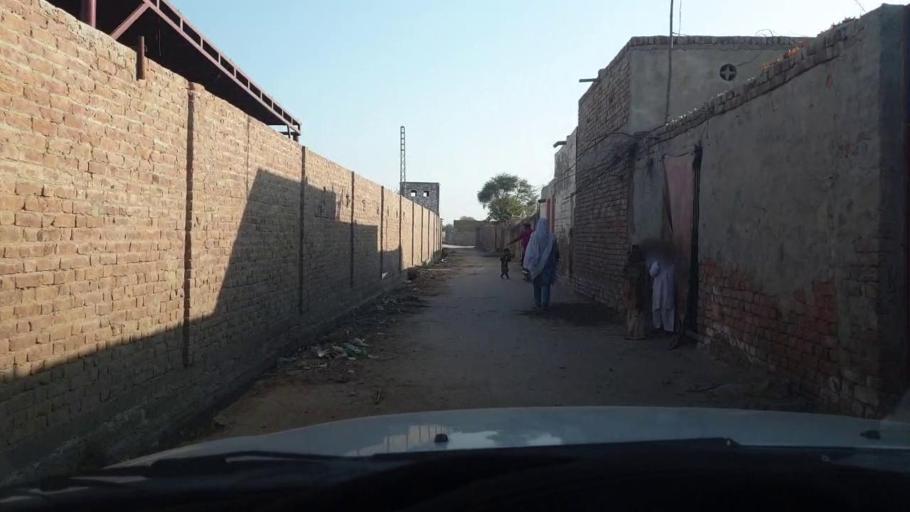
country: PK
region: Sindh
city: Mirpur Mathelo
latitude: 28.0194
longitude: 69.6037
